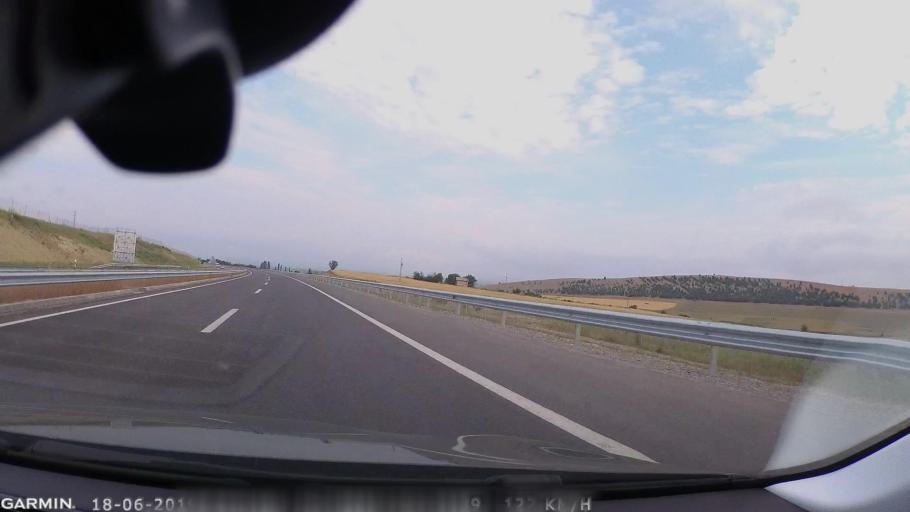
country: MK
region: Stip
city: Shtip
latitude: 41.7860
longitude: 22.1183
